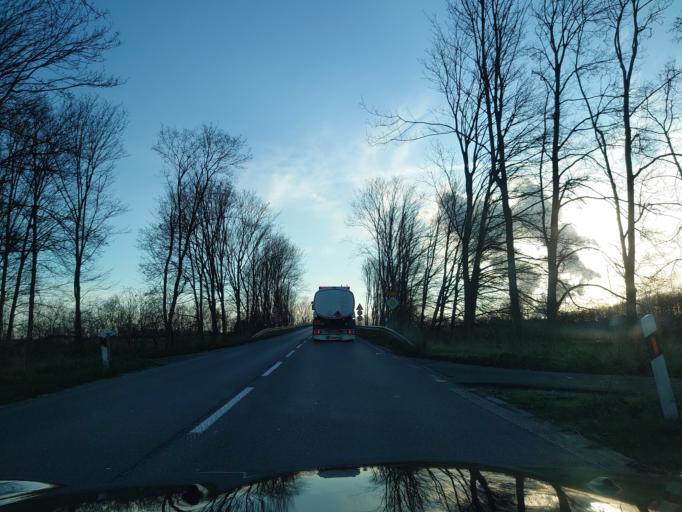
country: DE
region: North Rhine-Westphalia
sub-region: Regierungsbezirk Dusseldorf
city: Rommerskirchen
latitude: 51.0408
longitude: 6.7053
